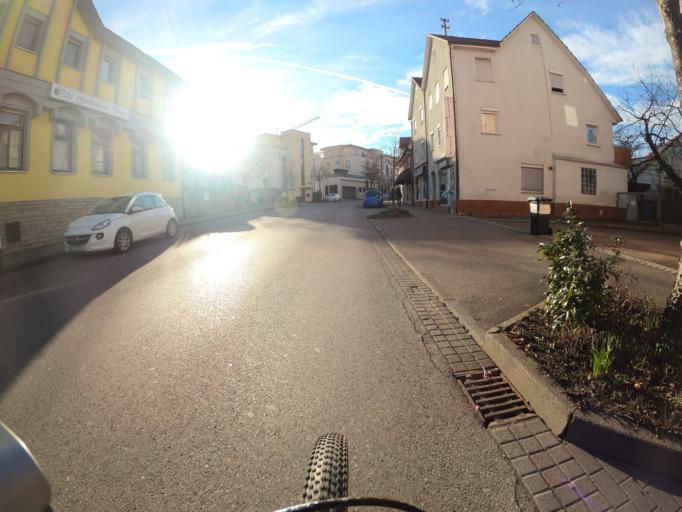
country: DE
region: Baden-Wuerttemberg
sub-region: Regierungsbezirk Stuttgart
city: Wendlingen am Neckar
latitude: 48.6747
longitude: 9.3836
